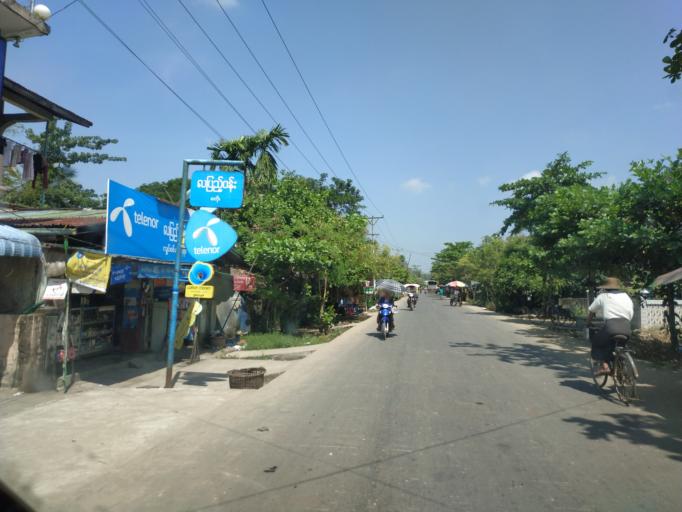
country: MM
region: Ayeyarwady
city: Mawlamyinegyunn
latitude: 16.3873
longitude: 95.2645
